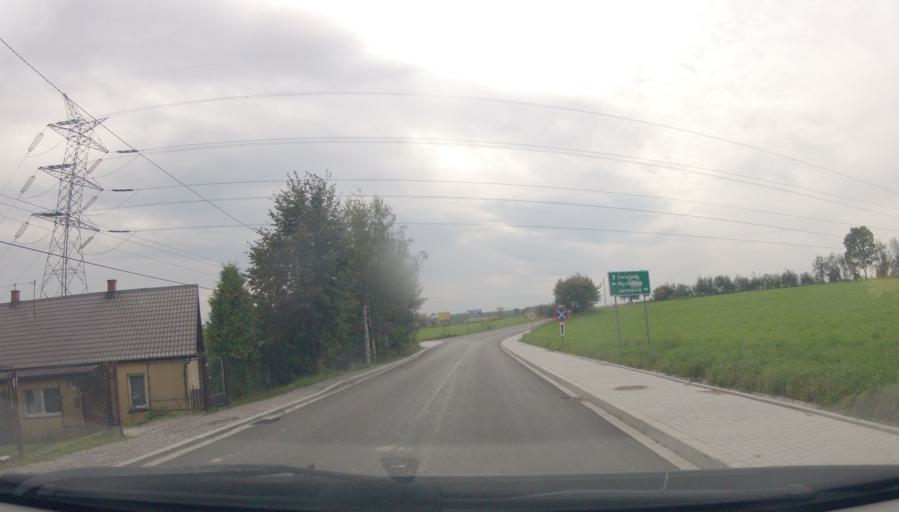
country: PL
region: Lesser Poland Voivodeship
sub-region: Powiat krakowski
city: Ochojno
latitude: 49.9450
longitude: 20.0066
